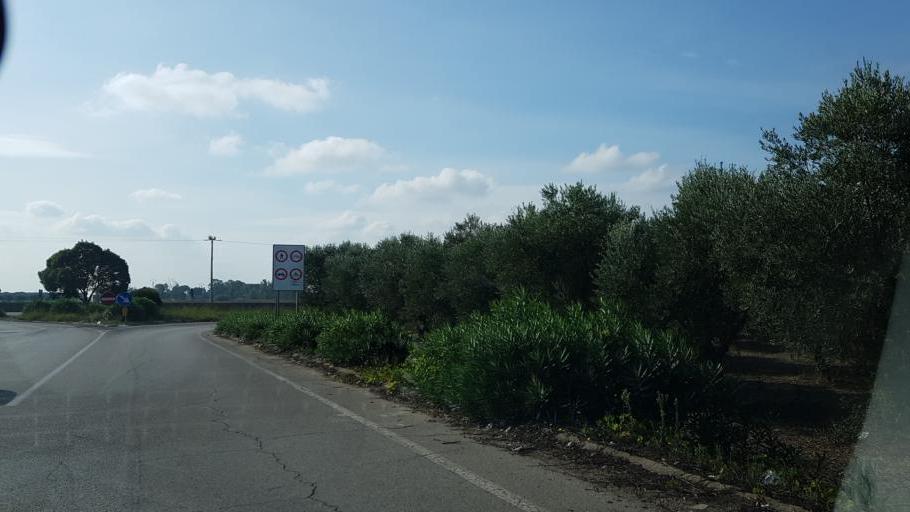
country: IT
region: Apulia
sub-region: Provincia di Brindisi
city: Brindisi
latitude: 40.6540
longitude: 17.9045
